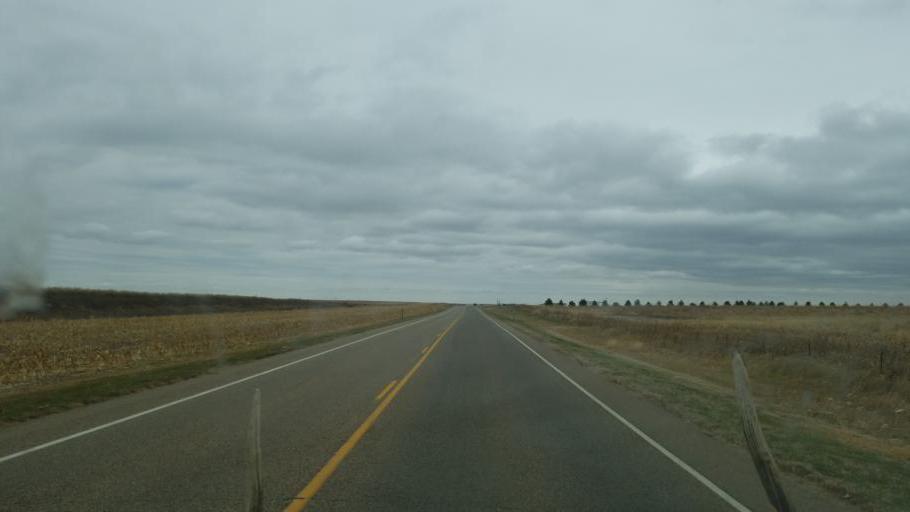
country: US
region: Colorado
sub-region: Cheyenne County
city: Cheyenne Wells
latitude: 38.8238
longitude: -102.3273
